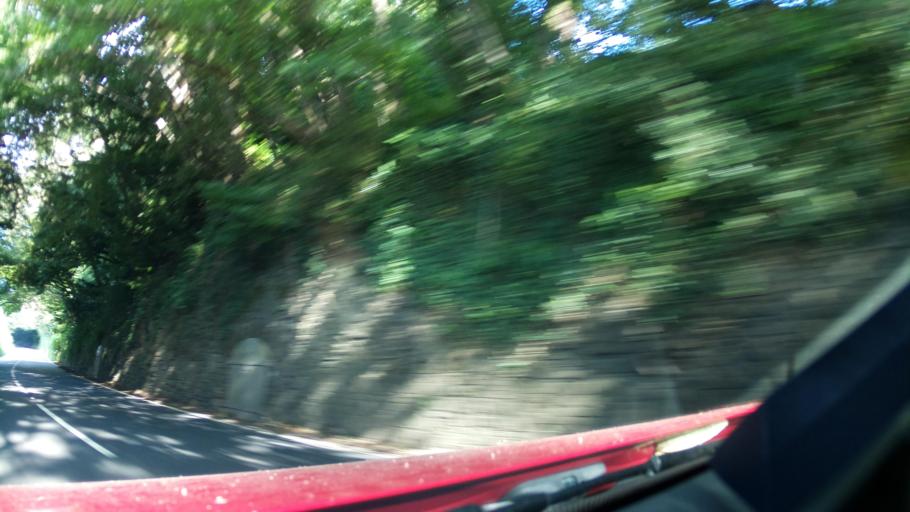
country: GB
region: England
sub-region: Devon
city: Exeter
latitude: 50.7500
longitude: -3.5431
